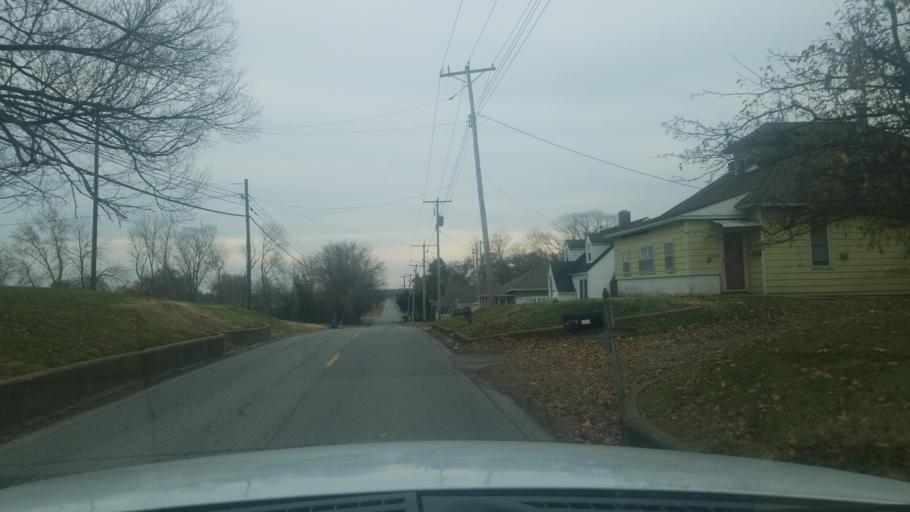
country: US
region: Illinois
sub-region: Saline County
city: Harrisburg
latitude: 37.7496
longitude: -88.5491
